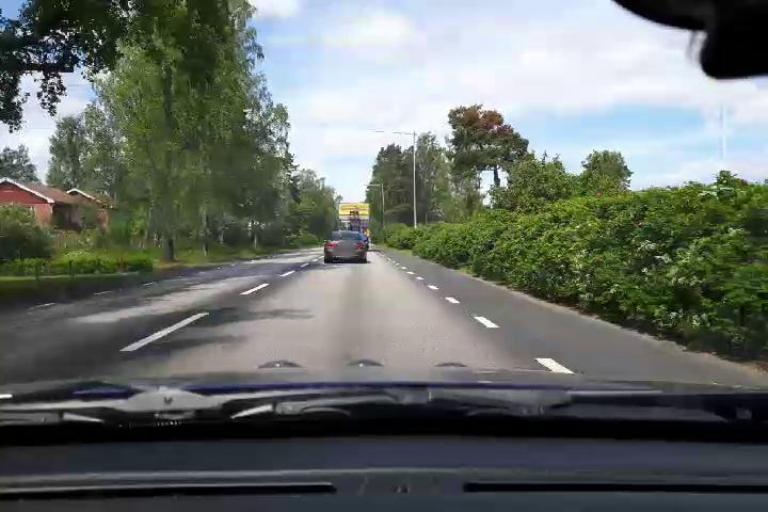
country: SE
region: Uppsala
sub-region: Osthammars Kommun
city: Bjorklinge
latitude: 60.0345
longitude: 17.5520
